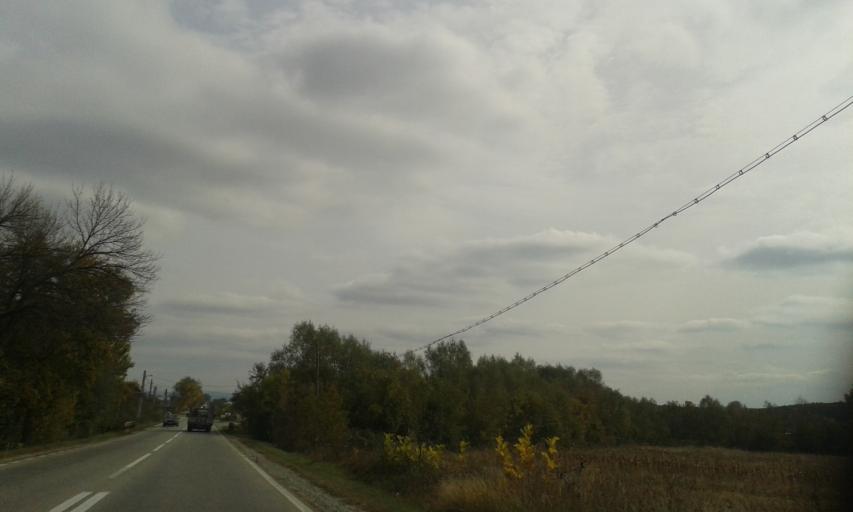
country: RO
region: Gorj
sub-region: Comuna Scoarta
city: Scoarta
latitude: 45.0308
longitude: 23.4175
